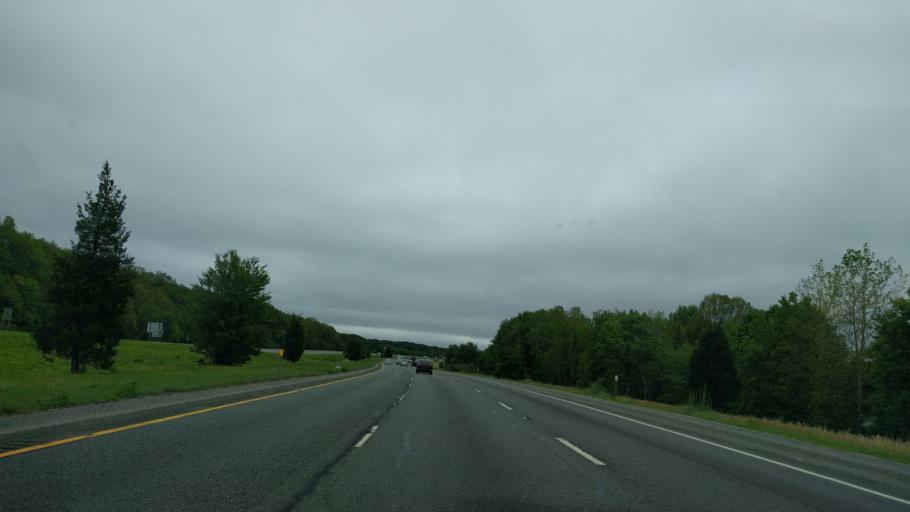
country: US
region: Rhode Island
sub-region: Providence County
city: Johnston
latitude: 41.8579
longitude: -71.5141
